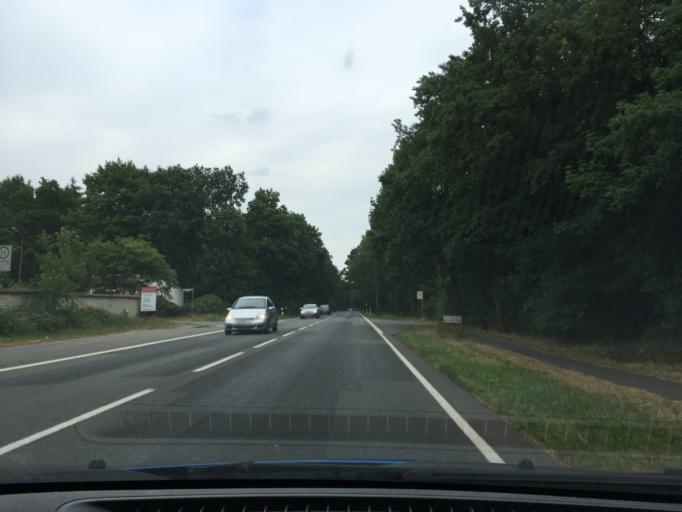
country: DE
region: Lower Saxony
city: Tostedt
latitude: 53.2955
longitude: 9.7376
